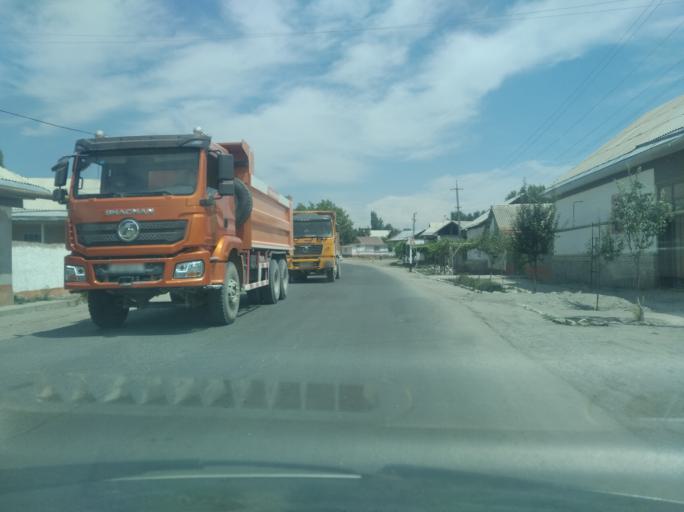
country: UZ
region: Andijon
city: Khujaobod
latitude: 40.6279
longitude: 72.4511
